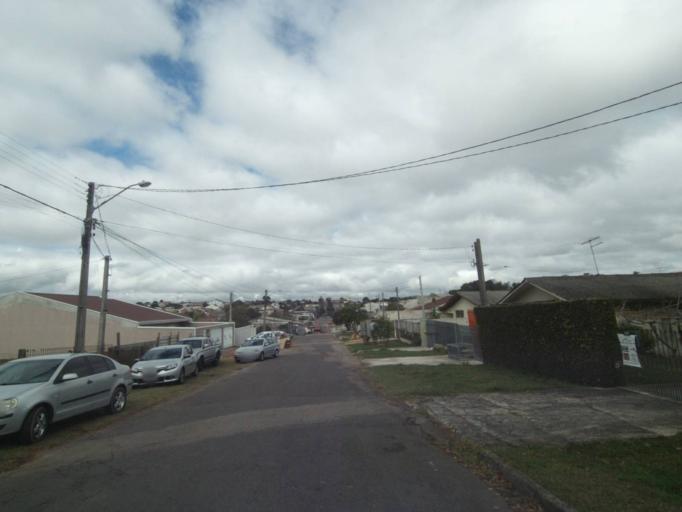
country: BR
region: Parana
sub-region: Sao Jose Dos Pinhais
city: Sao Jose dos Pinhais
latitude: -25.5392
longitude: -49.2897
